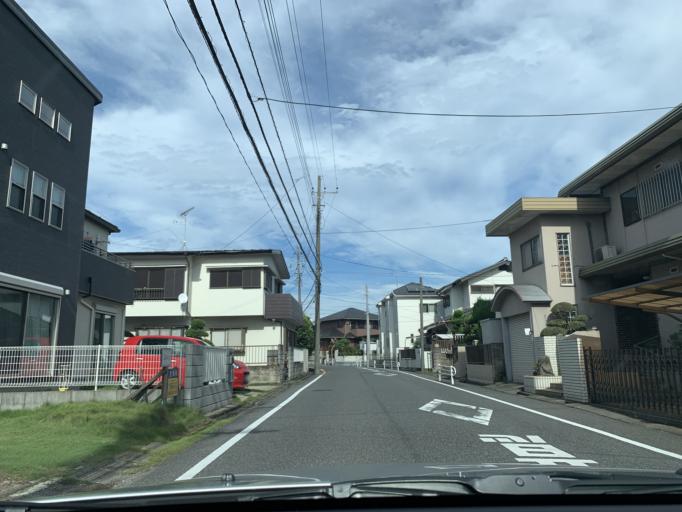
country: JP
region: Chiba
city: Nagareyama
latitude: 35.9034
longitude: 139.9262
